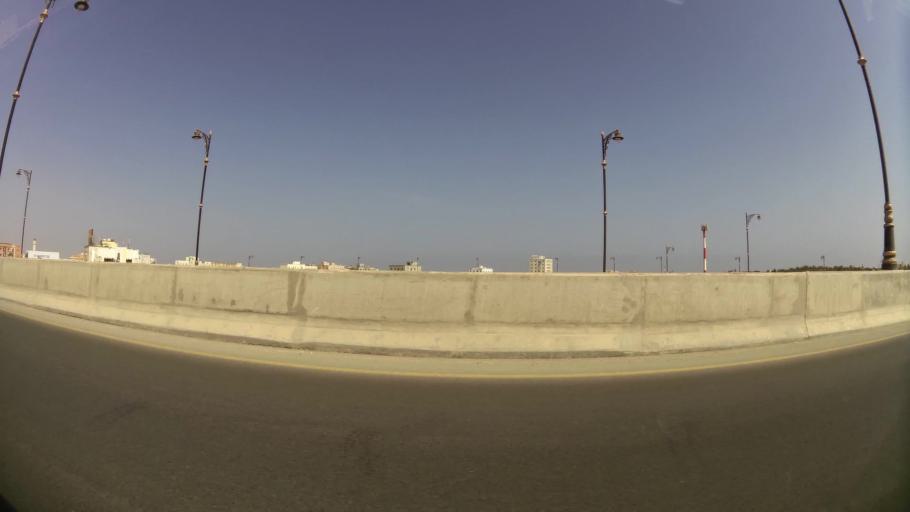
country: OM
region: Zufar
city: Salalah
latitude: 17.0165
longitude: 54.0570
